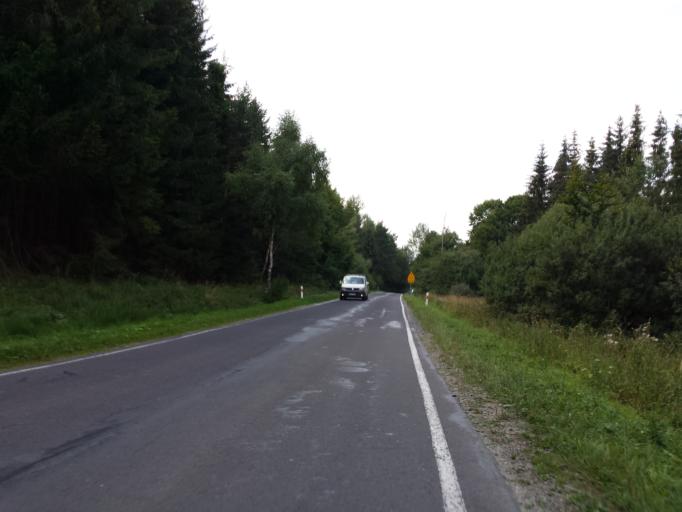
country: PL
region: Subcarpathian Voivodeship
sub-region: Powiat bieszczadzki
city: Lutowiska
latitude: 49.1398
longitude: 22.5438
